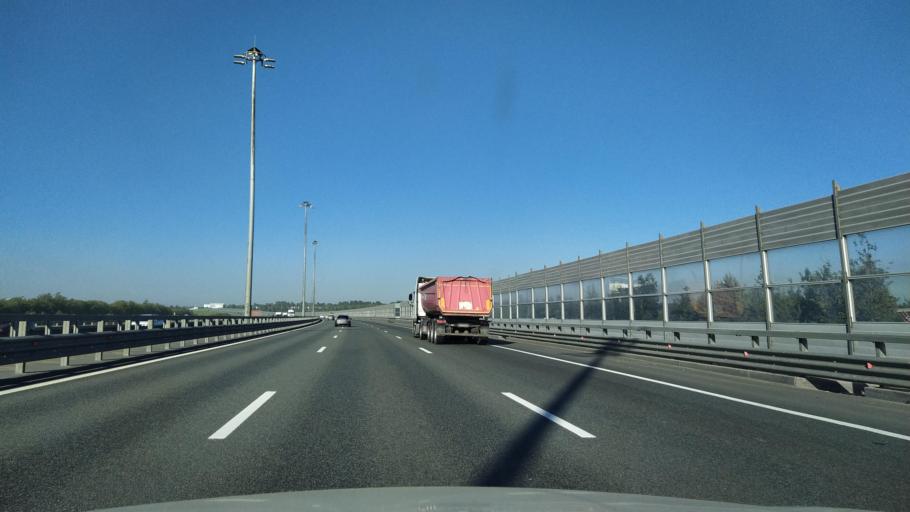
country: RU
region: St.-Petersburg
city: Levashovo
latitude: 60.0844
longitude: 30.2221
